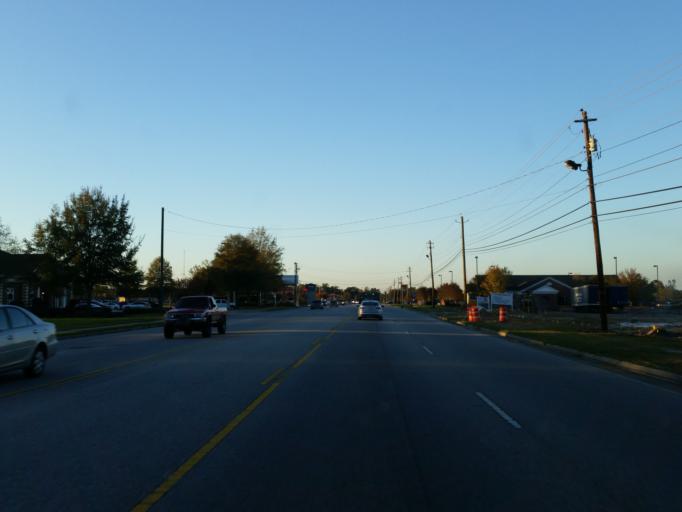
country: US
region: Georgia
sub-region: Lowndes County
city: Remerton
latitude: 30.8225
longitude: -83.3147
